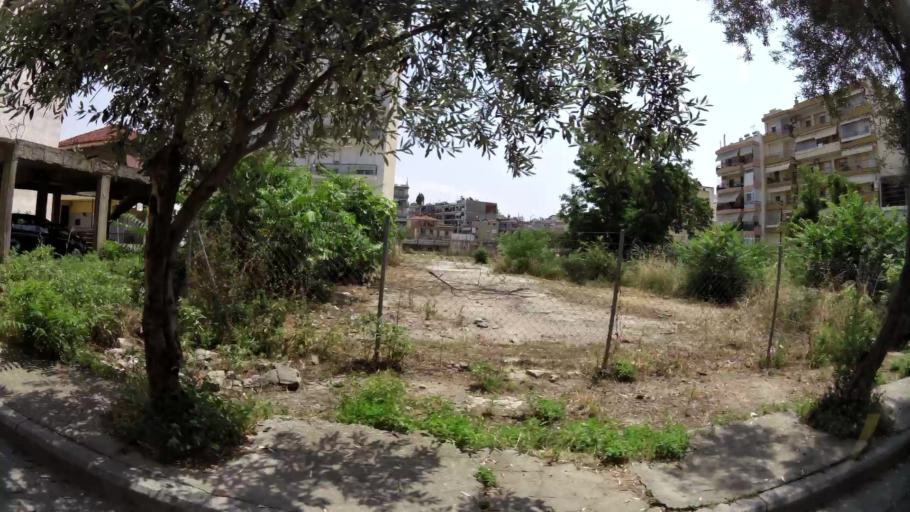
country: GR
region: Central Macedonia
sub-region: Nomos Thessalonikis
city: Menemeni
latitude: 40.6710
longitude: 22.8910
